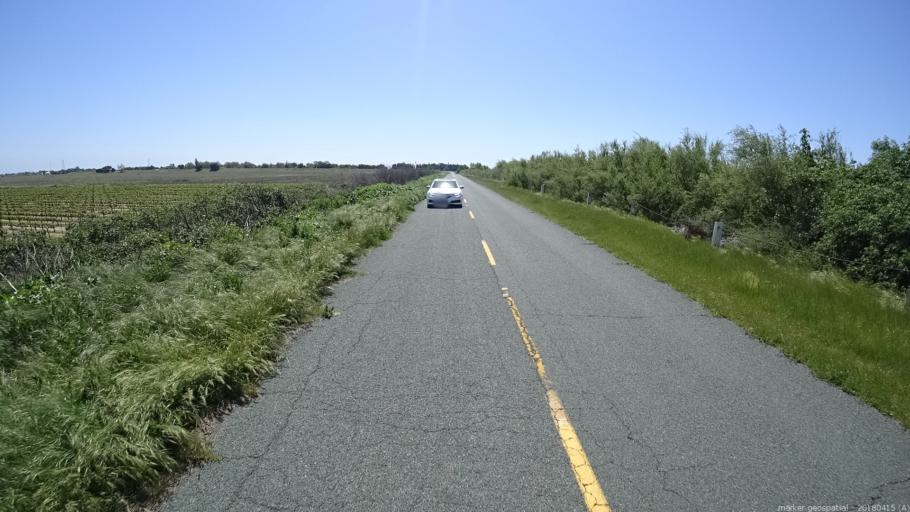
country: US
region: California
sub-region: Solano County
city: Rio Vista
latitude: 38.1796
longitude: -121.6477
